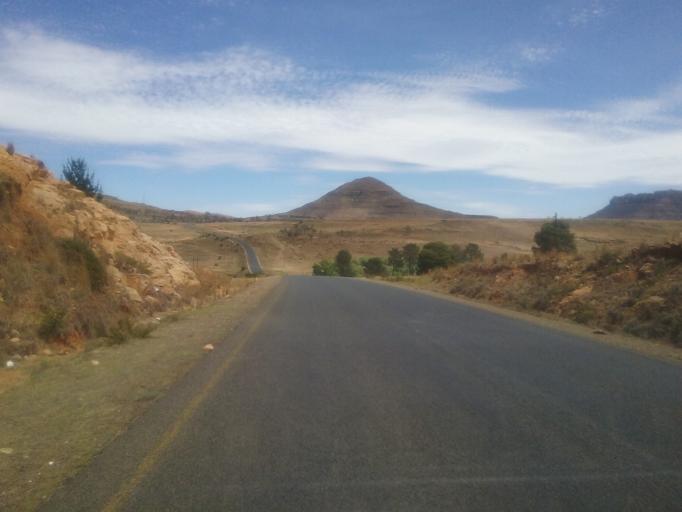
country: LS
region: Mafeteng
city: Mafeteng
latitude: -29.9656
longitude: 27.3027
